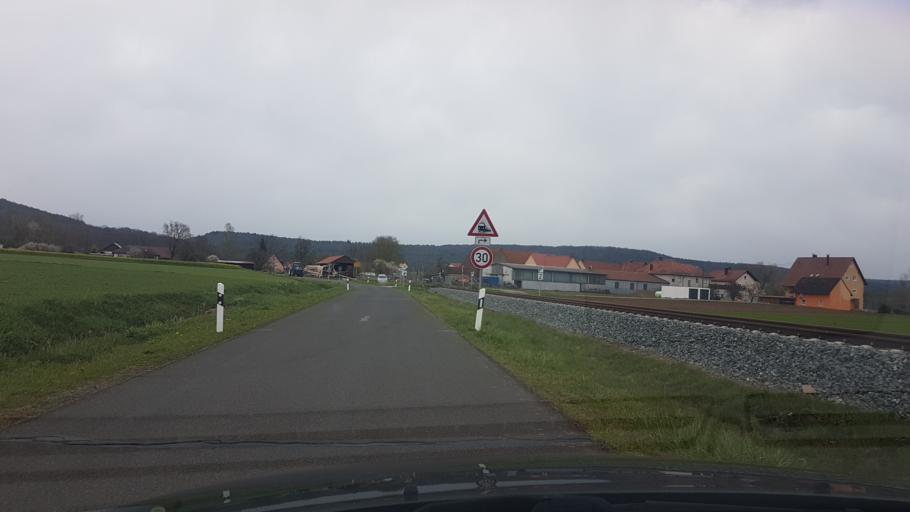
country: DE
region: Bavaria
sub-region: Upper Franconia
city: Reckendorf
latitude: 50.0398
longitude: 10.8301
